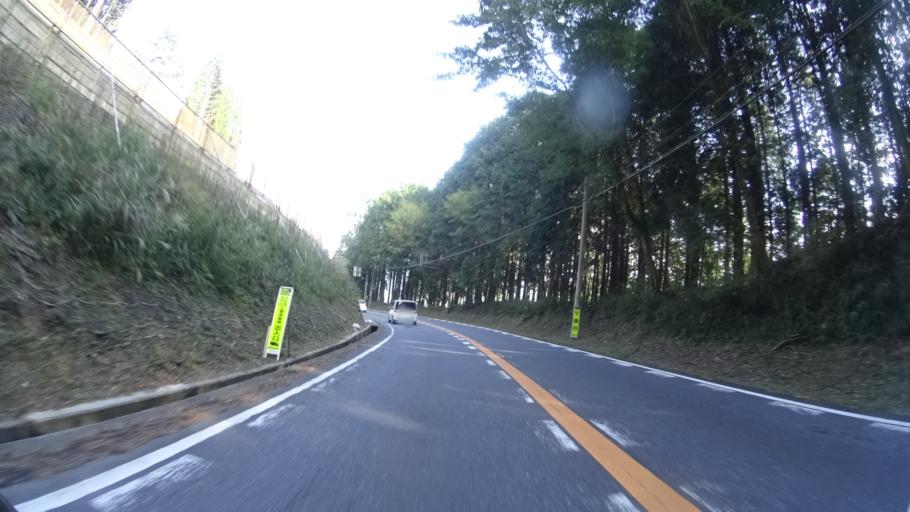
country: JP
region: Oita
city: Tsukawaki
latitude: 33.2611
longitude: 131.3266
